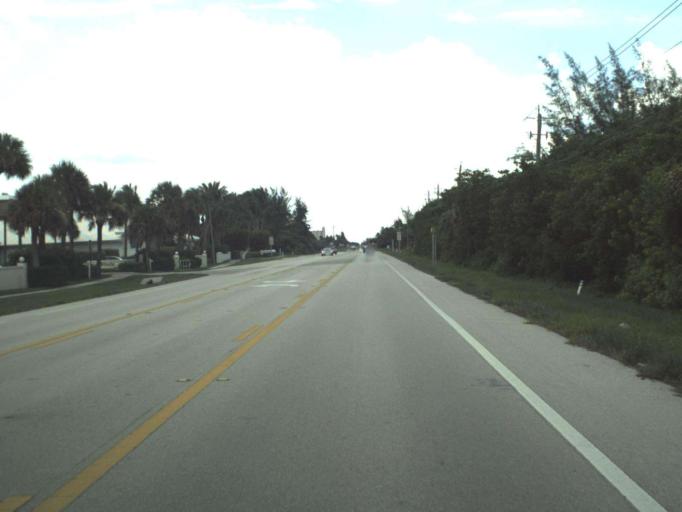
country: US
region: Florida
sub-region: Saint Lucie County
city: Hutchinson Island South
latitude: 27.2808
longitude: -80.2099
